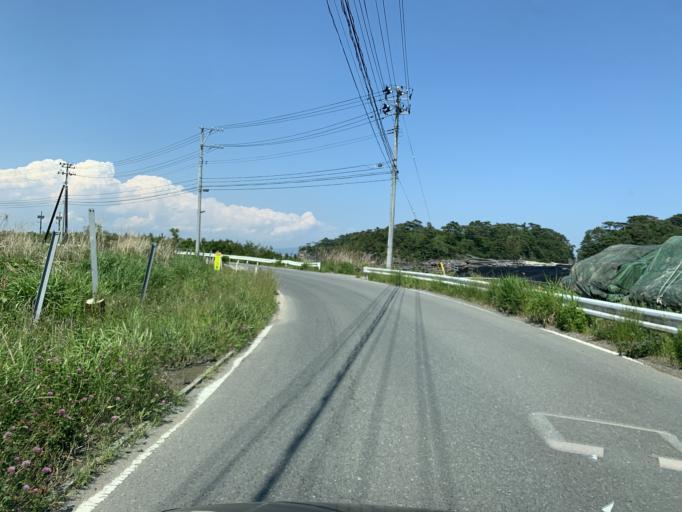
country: JP
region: Miyagi
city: Yamoto
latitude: 38.3516
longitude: 141.1574
